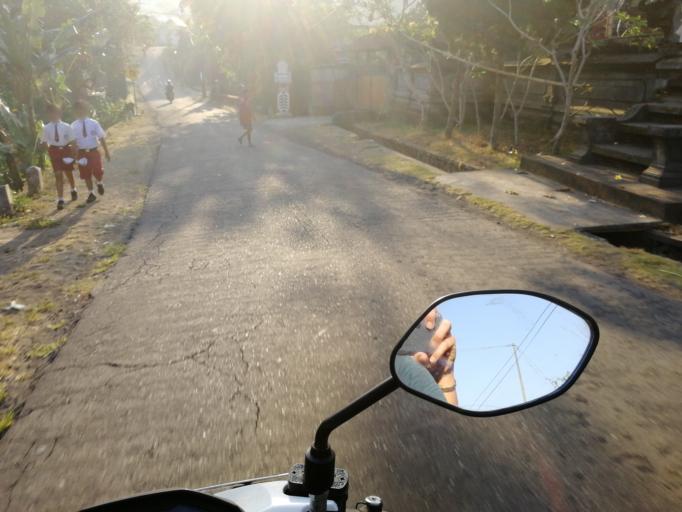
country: ID
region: Bali
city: Tistagede
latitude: -8.3875
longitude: 115.6150
